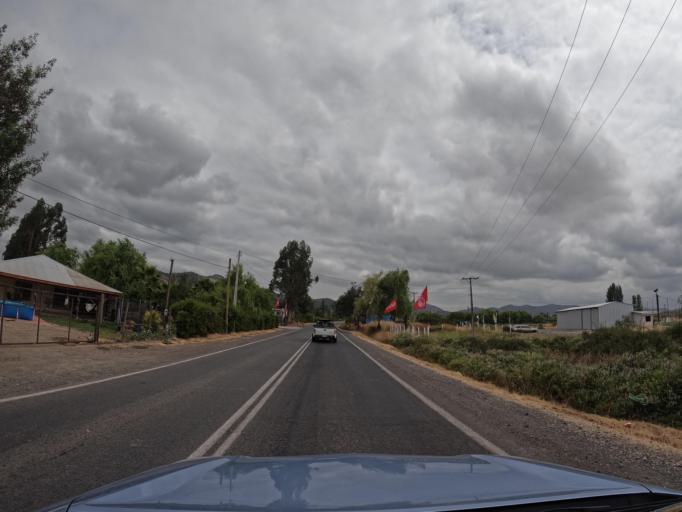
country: CL
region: Maule
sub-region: Provincia de Curico
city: Teno
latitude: -34.8554
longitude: -71.1917
